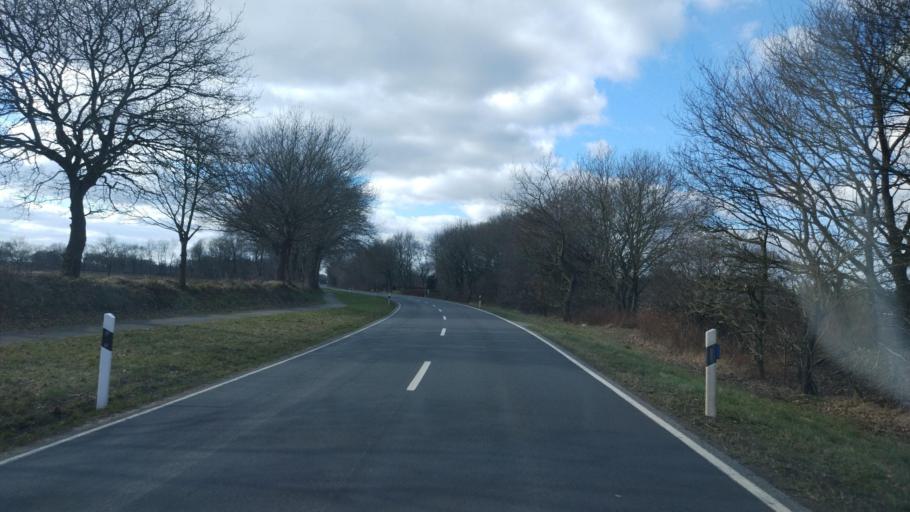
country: DE
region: Schleswig-Holstein
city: Gross Rheide
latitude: 54.4477
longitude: 9.4037
